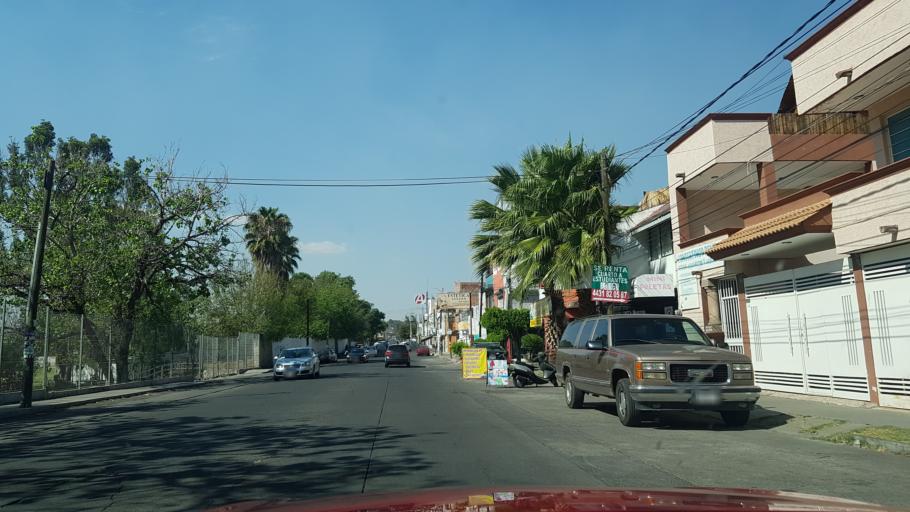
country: MX
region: Michoacan
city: Morelia
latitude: 19.7002
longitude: -101.1669
